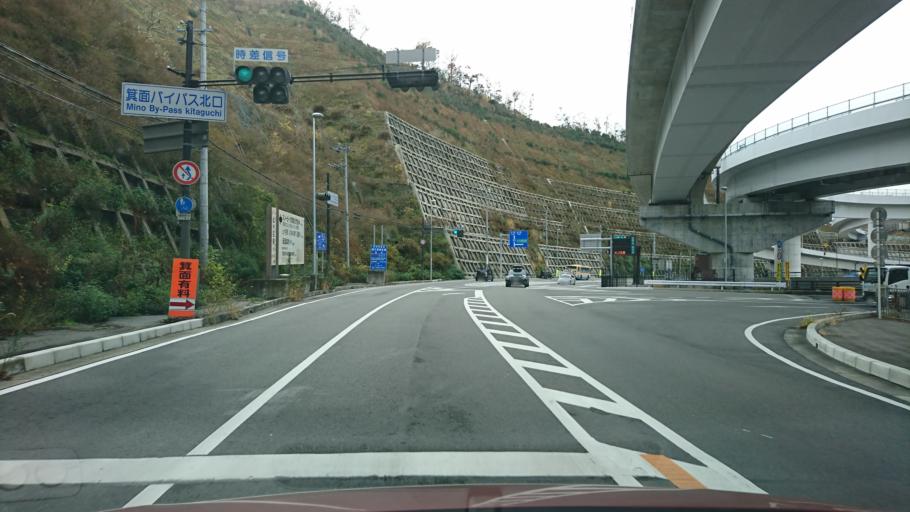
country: JP
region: Osaka
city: Mino
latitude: 34.8754
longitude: 135.4559
